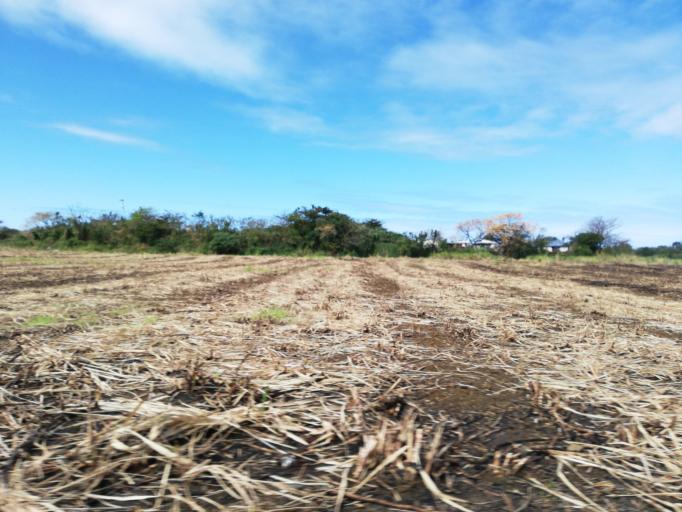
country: MU
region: Grand Port
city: Plaine Magnien
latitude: -20.4636
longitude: 57.6722
